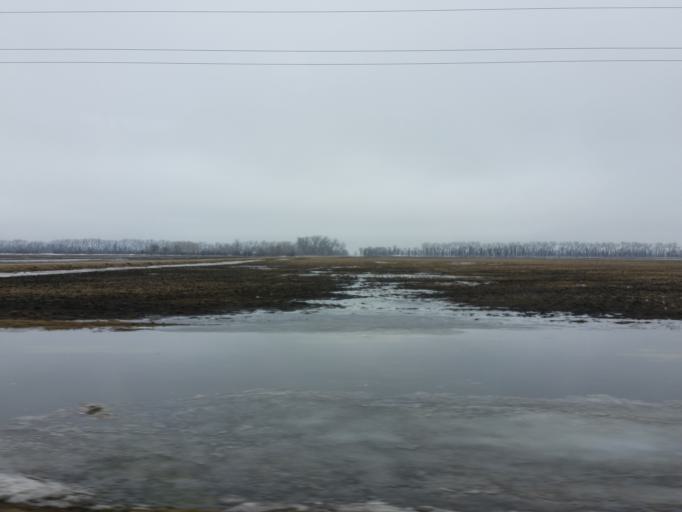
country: US
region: North Dakota
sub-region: Walsh County
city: Grafton
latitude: 48.5720
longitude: -97.4248
